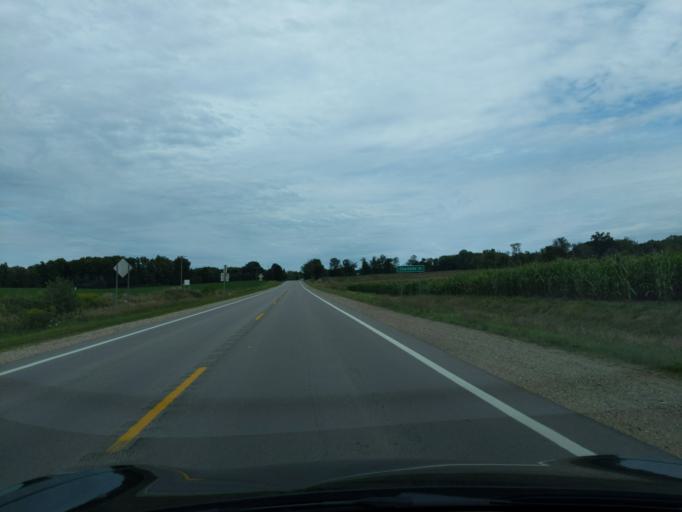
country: US
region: Michigan
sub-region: Barry County
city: Nashville
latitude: 42.5671
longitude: -85.0917
